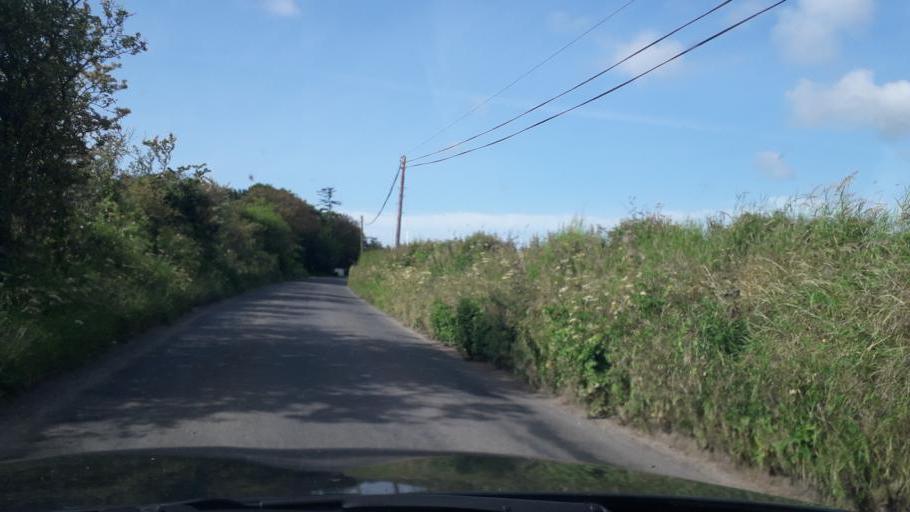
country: IE
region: Leinster
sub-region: Loch Garman
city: Loch Garman
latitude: 52.2408
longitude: -6.5501
